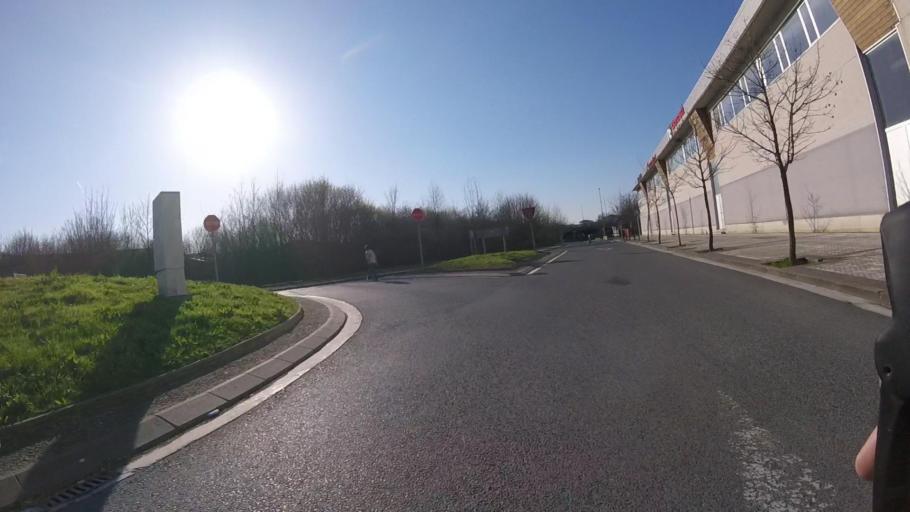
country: ES
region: Basque Country
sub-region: Provincia de Guipuzcoa
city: Astigarraga
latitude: 43.2715
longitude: -1.9552
